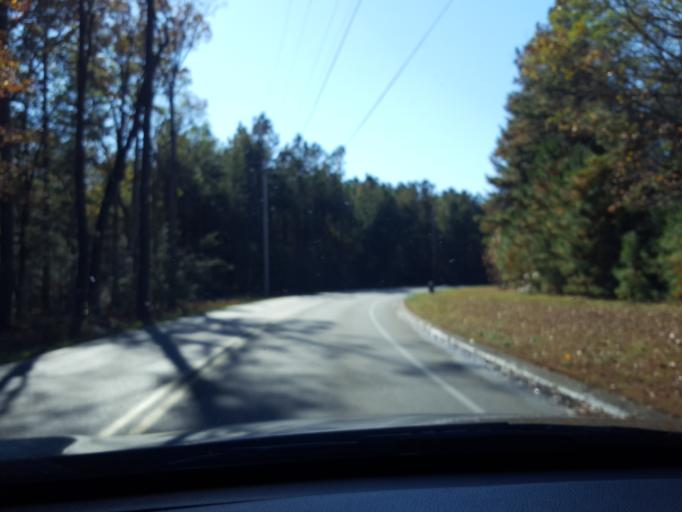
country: US
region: Maryland
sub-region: Saint Mary's County
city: Leonardtown
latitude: 38.2798
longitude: -76.5819
